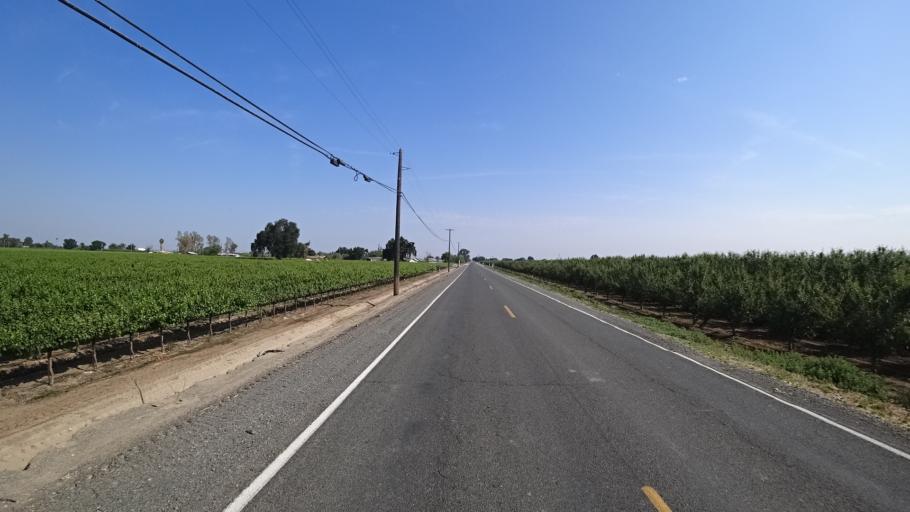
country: US
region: California
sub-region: Fresno County
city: Riverdale
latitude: 36.3490
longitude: -119.8513
